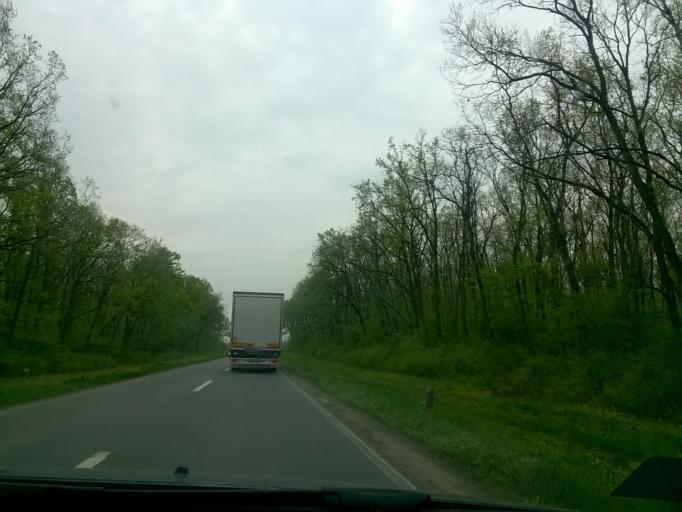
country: RS
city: Hrtkovci
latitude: 44.8961
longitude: 19.7642
